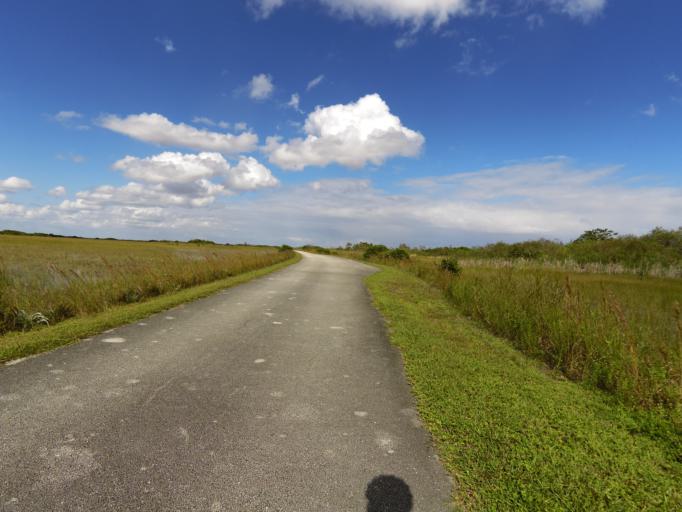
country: US
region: Florida
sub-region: Miami-Dade County
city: The Hammocks
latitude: 25.7230
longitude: -80.7597
